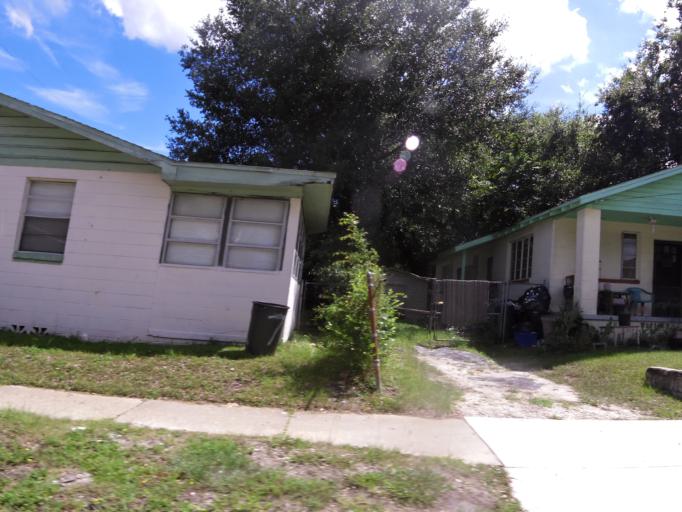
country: US
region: Florida
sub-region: Duval County
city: Jacksonville
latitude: 30.3847
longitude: -81.6428
